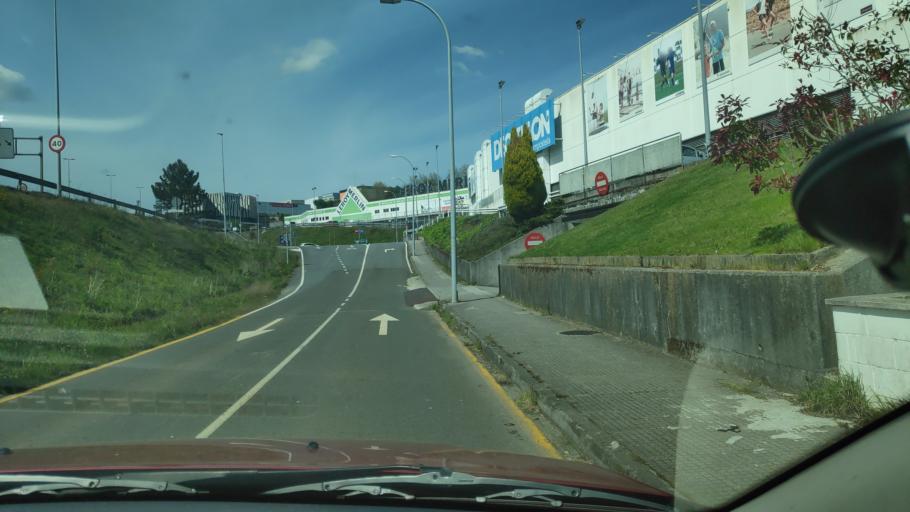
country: ES
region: Galicia
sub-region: Provincia da Coruna
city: Santiago de Compostela
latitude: 42.9014
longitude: -8.5107
